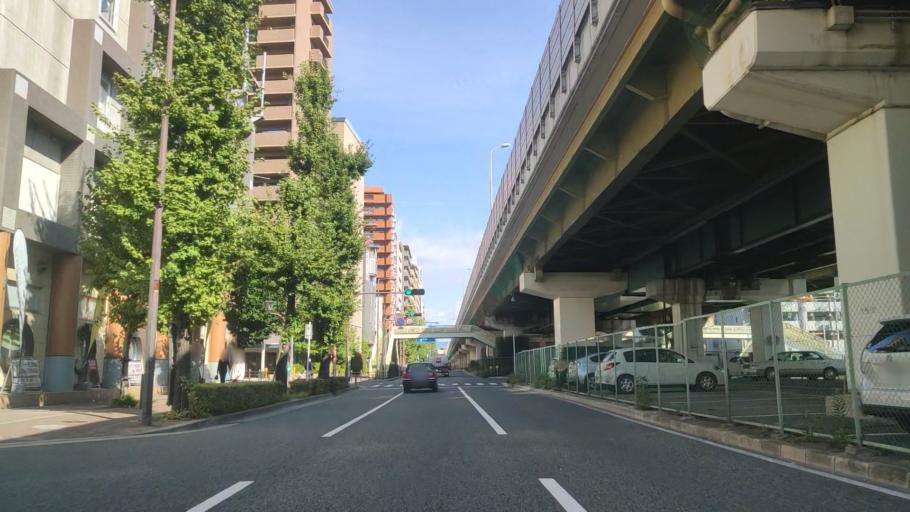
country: JP
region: Osaka
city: Suita
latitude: 34.7427
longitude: 135.4982
